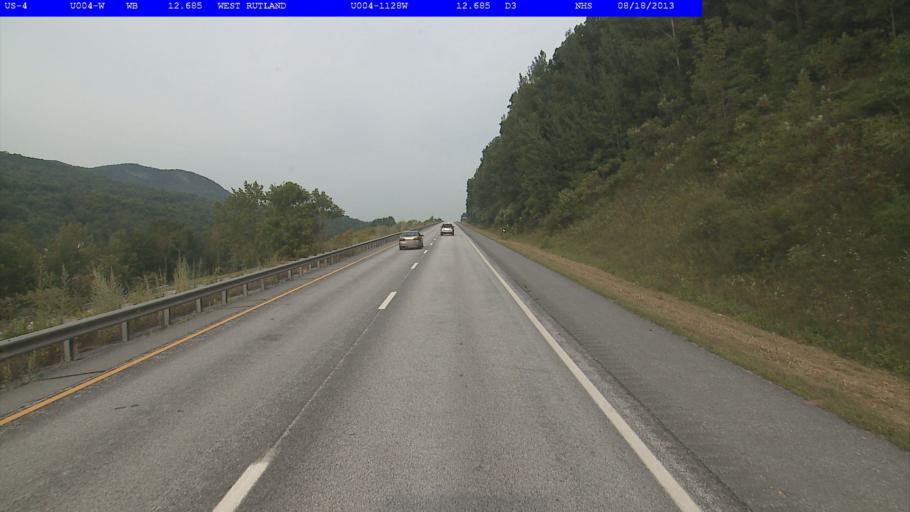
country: US
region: Vermont
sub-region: Rutland County
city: West Rutland
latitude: 43.6067
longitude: -73.0715
